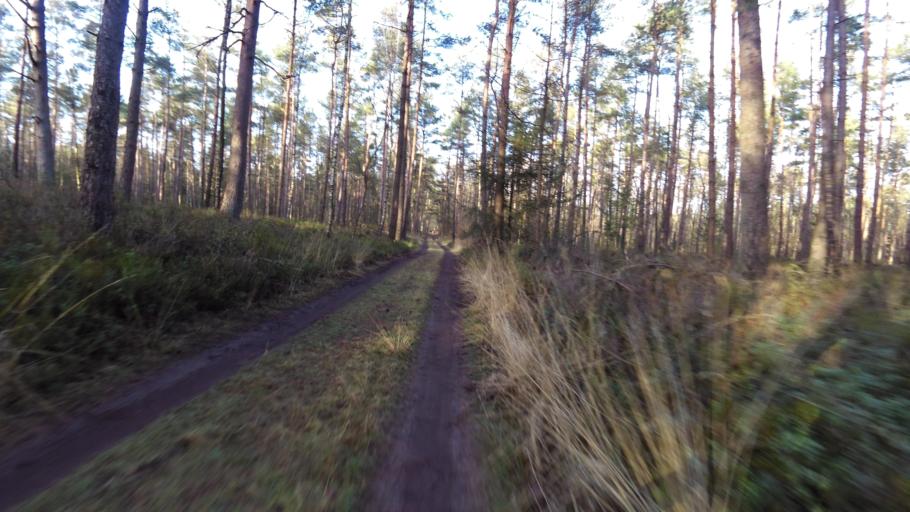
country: NL
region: Gelderland
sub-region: Gemeente Epe
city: Vaassen
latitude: 52.2636
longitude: 5.9133
